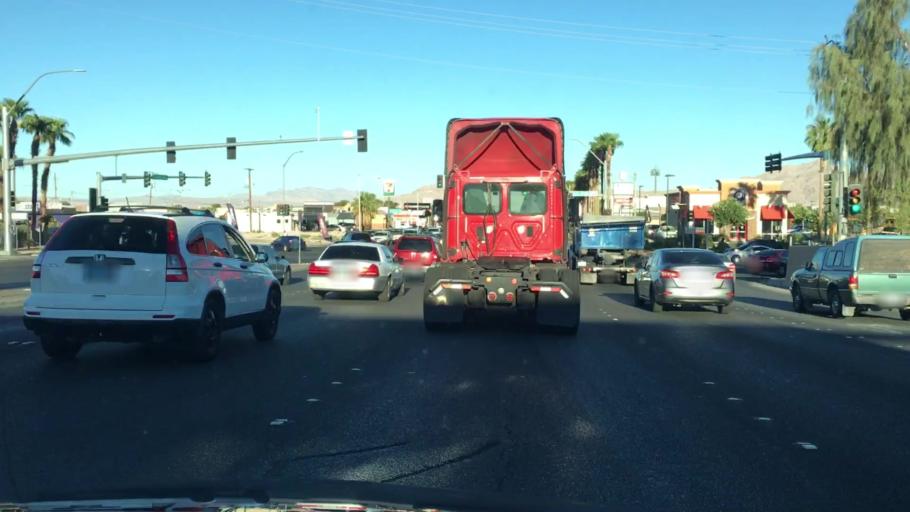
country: US
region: Nevada
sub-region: Clark County
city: North Las Vegas
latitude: 36.2176
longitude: -115.1217
